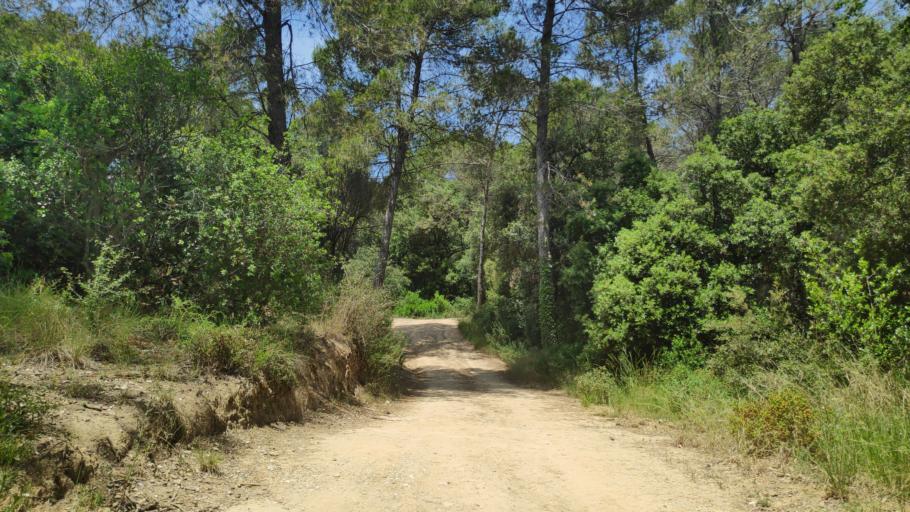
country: ES
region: Catalonia
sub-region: Provincia de Barcelona
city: Rubi
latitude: 41.5025
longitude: 2.0598
